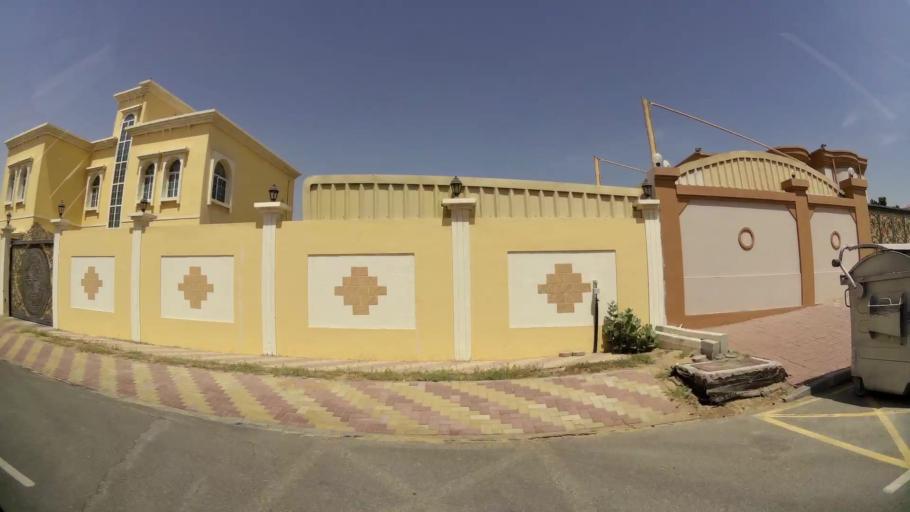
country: AE
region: Ash Shariqah
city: Sharjah
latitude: 25.1777
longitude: 55.4250
